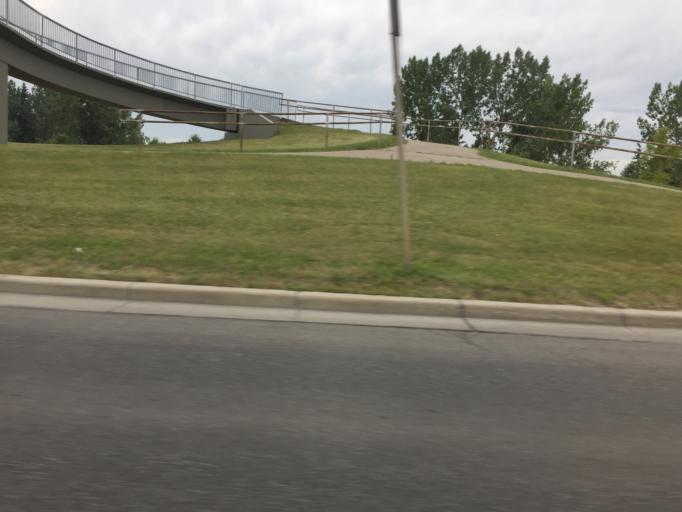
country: CA
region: Alberta
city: Calgary
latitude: 51.0247
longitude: -114.1231
